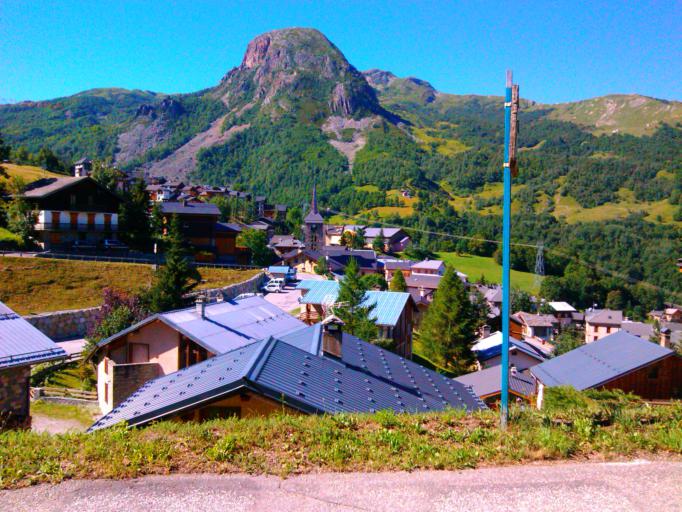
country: FR
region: Rhone-Alpes
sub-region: Departement de la Savoie
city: Saint-Martin-de-Belleville
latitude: 45.3816
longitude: 6.5055
